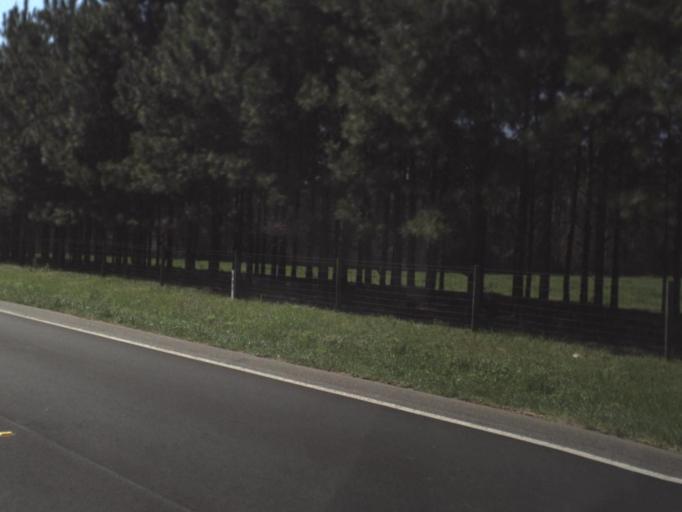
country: US
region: Florida
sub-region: Jackson County
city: Marianna
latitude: 30.6871
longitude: -85.1773
